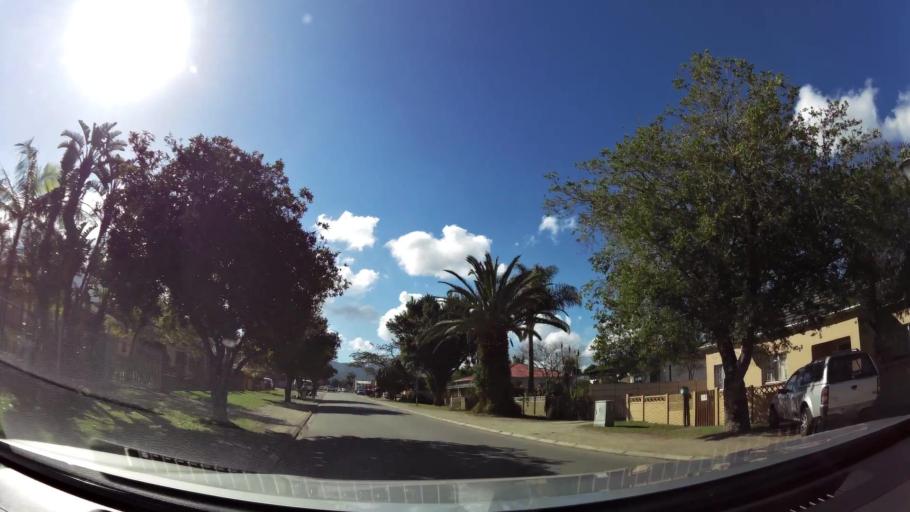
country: ZA
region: Western Cape
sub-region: Eden District Municipality
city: George
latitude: -33.9660
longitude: 22.4636
